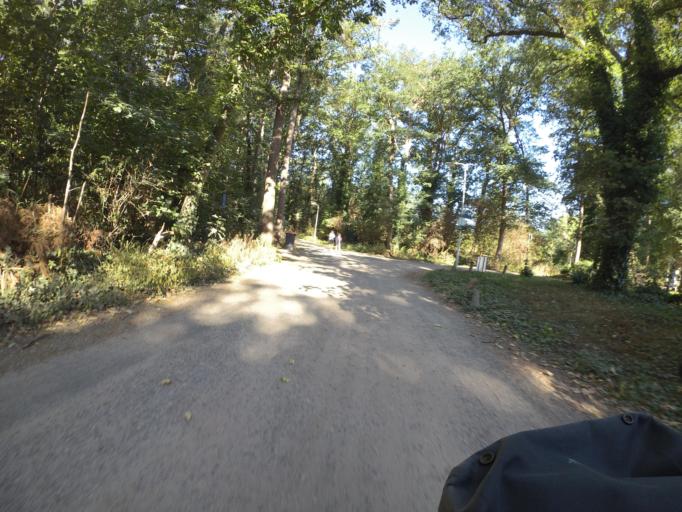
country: NL
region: Gelderland
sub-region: Gemeente Lochem
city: Lochem
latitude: 52.1498
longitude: 6.4109
